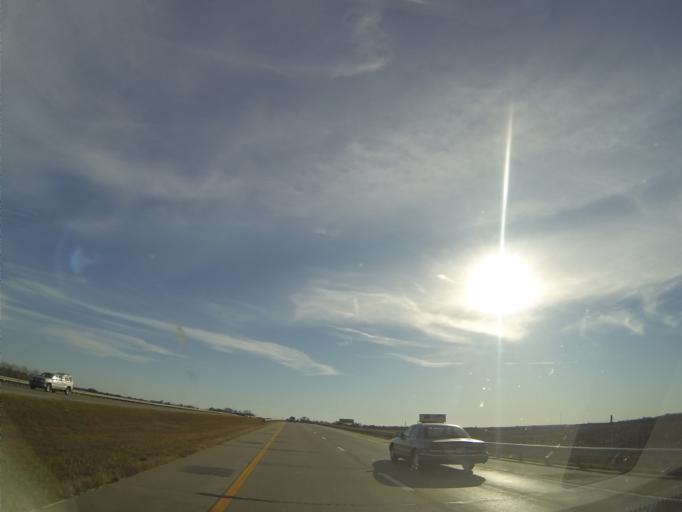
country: US
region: Kansas
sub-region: Saline County
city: Salina
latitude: 38.8539
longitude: -97.6466
